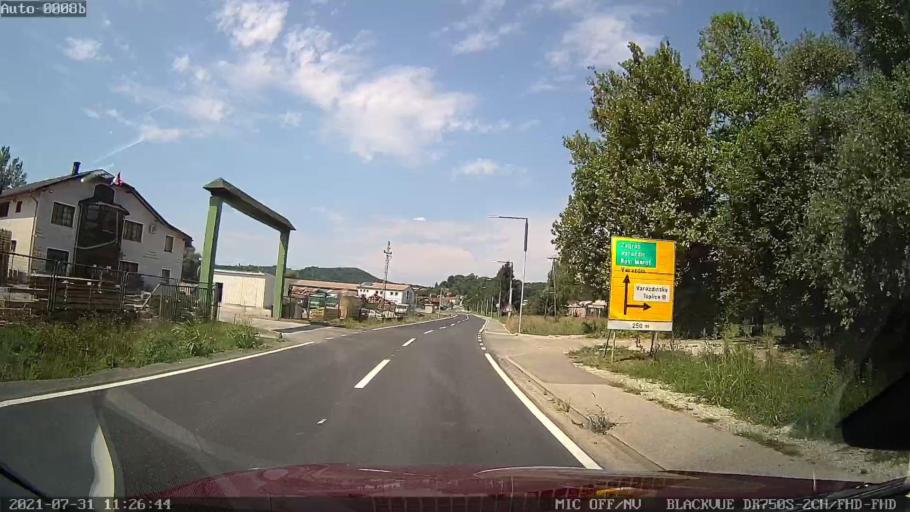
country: HR
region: Varazdinska
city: Jalzabet
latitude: 46.2109
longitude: 16.4377
